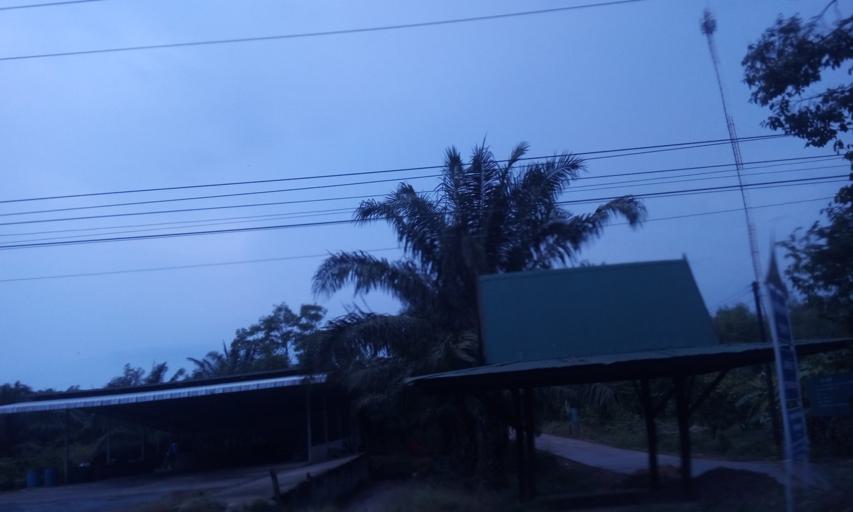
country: TH
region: Trat
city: Khao Saming
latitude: 12.3417
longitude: 102.3741
